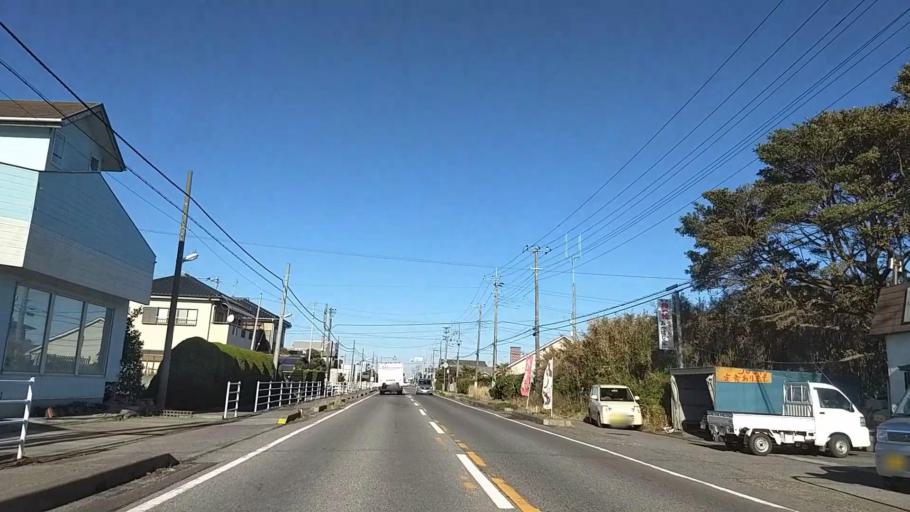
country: JP
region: Chiba
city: Togane
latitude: 35.4906
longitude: 140.4230
